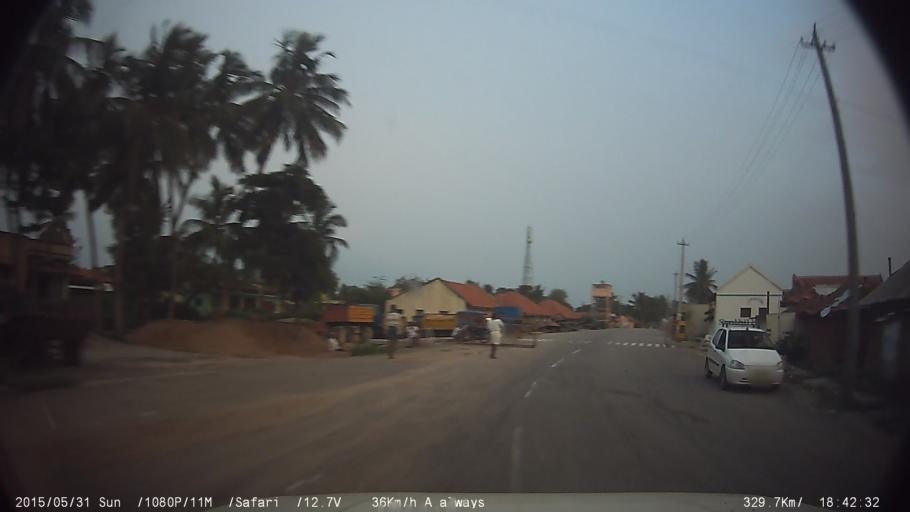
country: IN
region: Karnataka
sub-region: Mysore
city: Tirumakudal Narsipur
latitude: 12.1525
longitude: 76.8012
